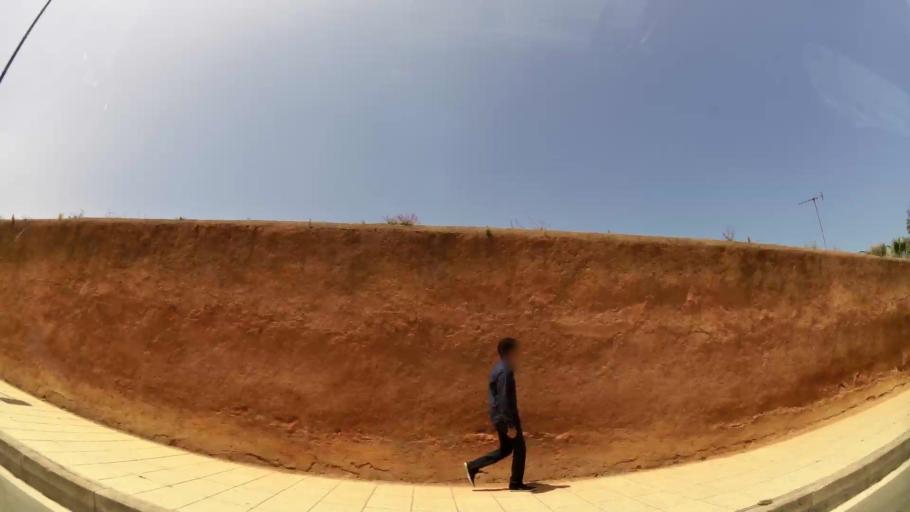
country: MA
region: Rabat-Sale-Zemmour-Zaer
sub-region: Rabat
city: Rabat
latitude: 34.0111
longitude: -6.8313
